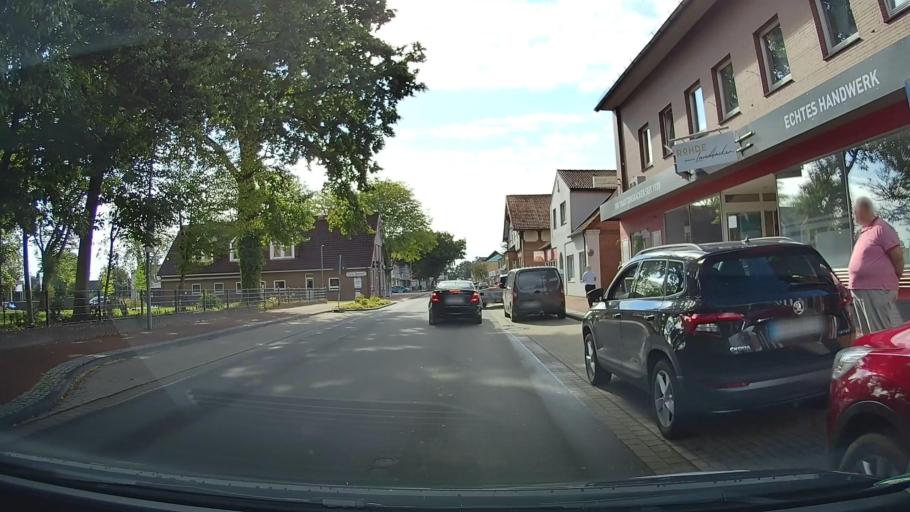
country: DE
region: Lower Saxony
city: Gnarrenburg
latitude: 53.3818
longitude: 9.0033
